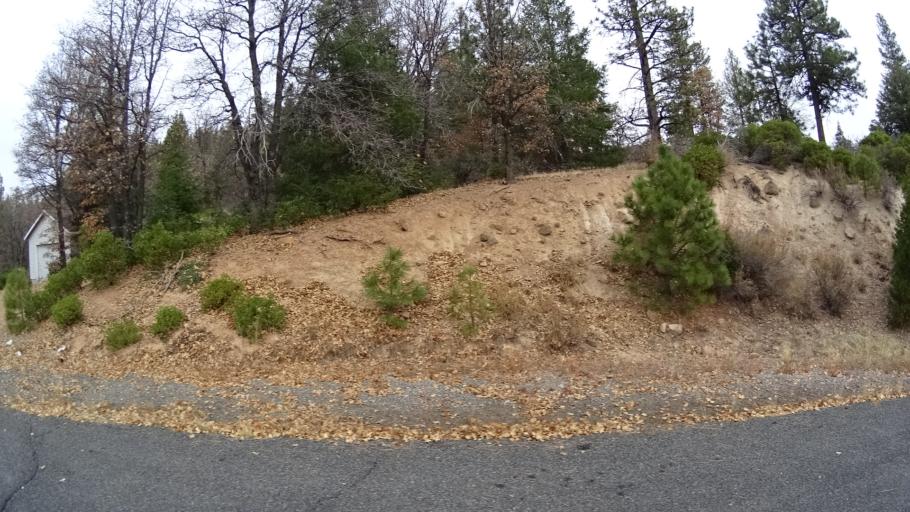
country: US
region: California
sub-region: Siskiyou County
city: Weed
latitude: 41.4136
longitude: -122.3733
